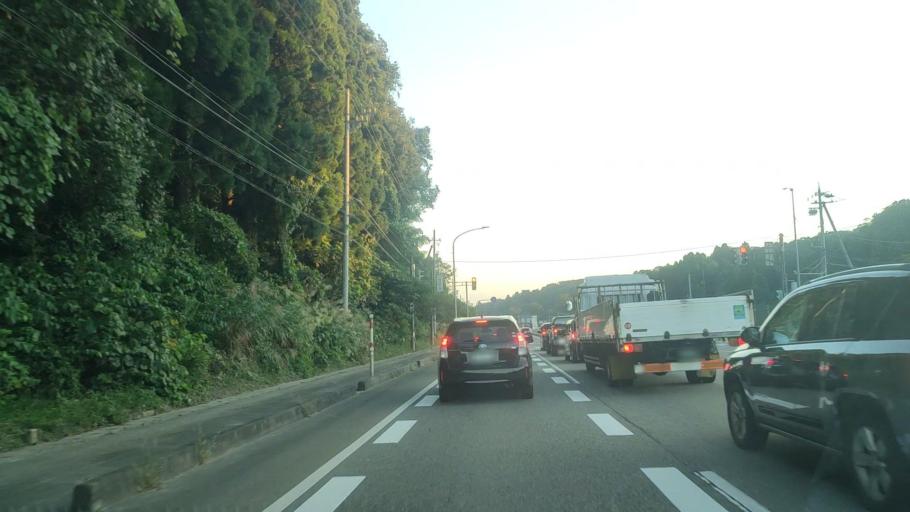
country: JP
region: Toyama
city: Takaoka
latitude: 36.7897
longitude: 137.0009
